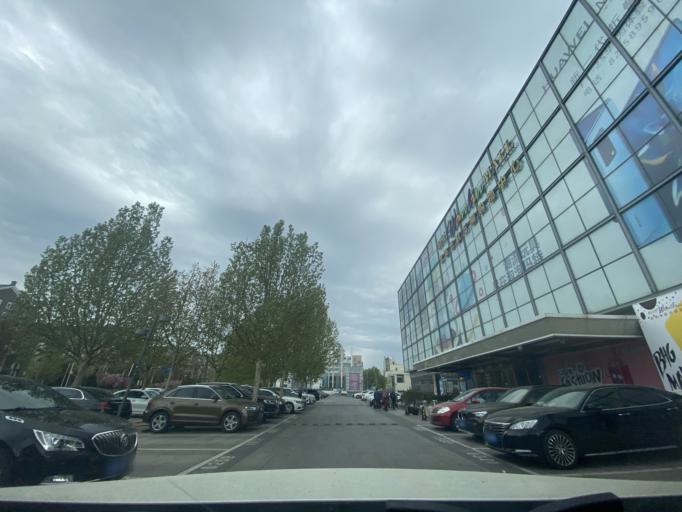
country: CN
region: Beijing
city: Haidian
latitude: 39.9719
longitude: 116.2897
